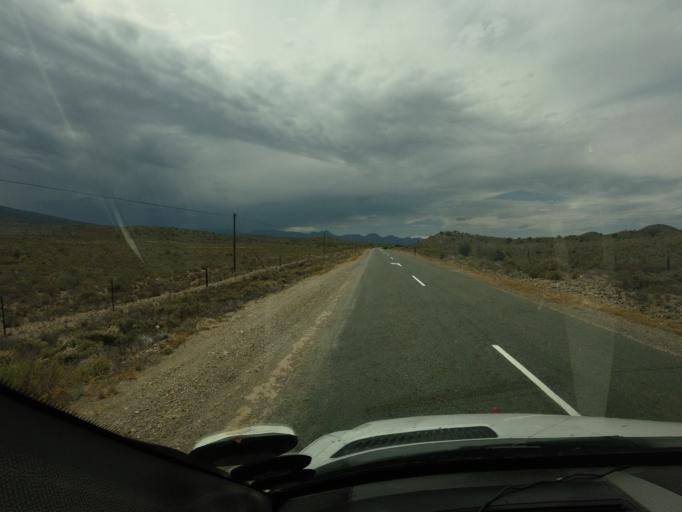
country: ZA
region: Western Cape
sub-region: Eden District Municipality
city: Ladismith
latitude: -33.6112
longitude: 21.0652
